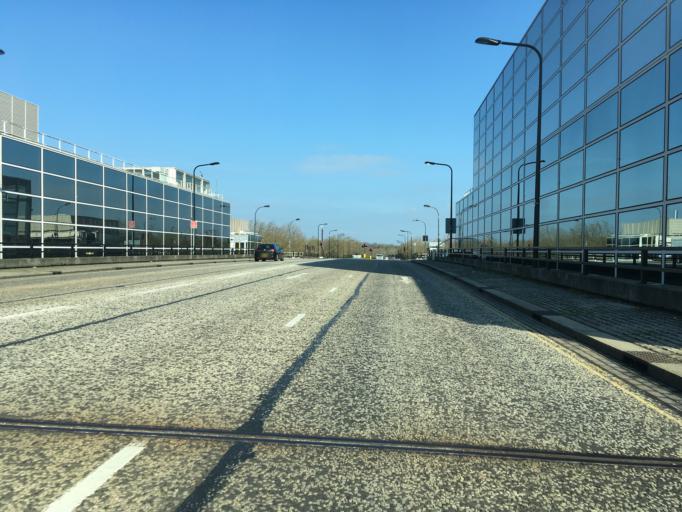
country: GB
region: England
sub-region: Milton Keynes
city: Milton Keynes
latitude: 52.0437
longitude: -0.7546
